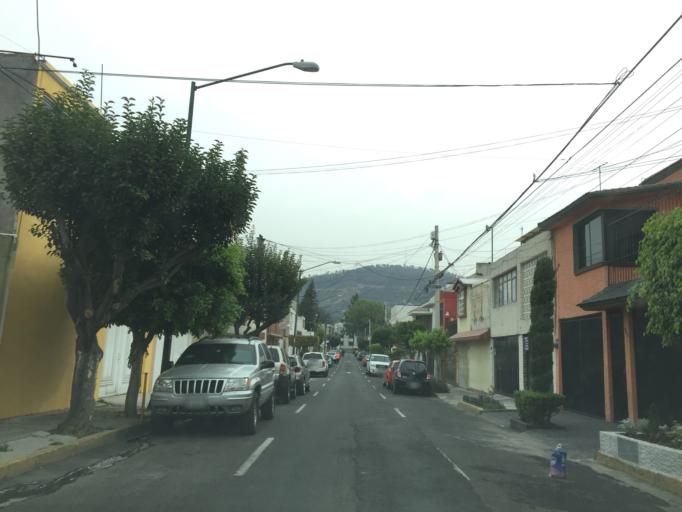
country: MX
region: Mexico
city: Colonia Lindavista
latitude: 19.4980
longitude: -99.1265
